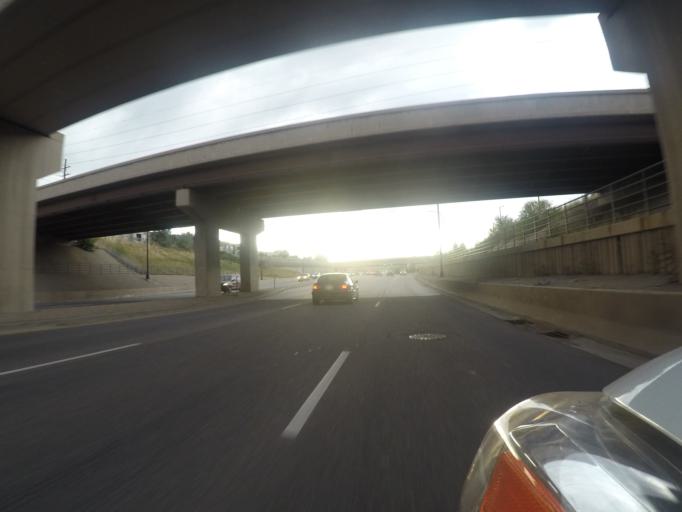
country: US
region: Colorado
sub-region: Arapahoe County
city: Littleton
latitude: 39.6242
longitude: -105.0105
